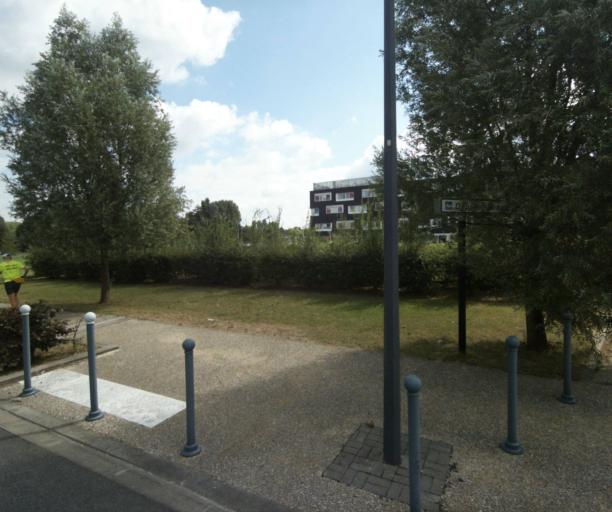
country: FR
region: Nord-Pas-de-Calais
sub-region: Departement du Nord
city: Wasquehal
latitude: 50.6535
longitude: 3.1508
